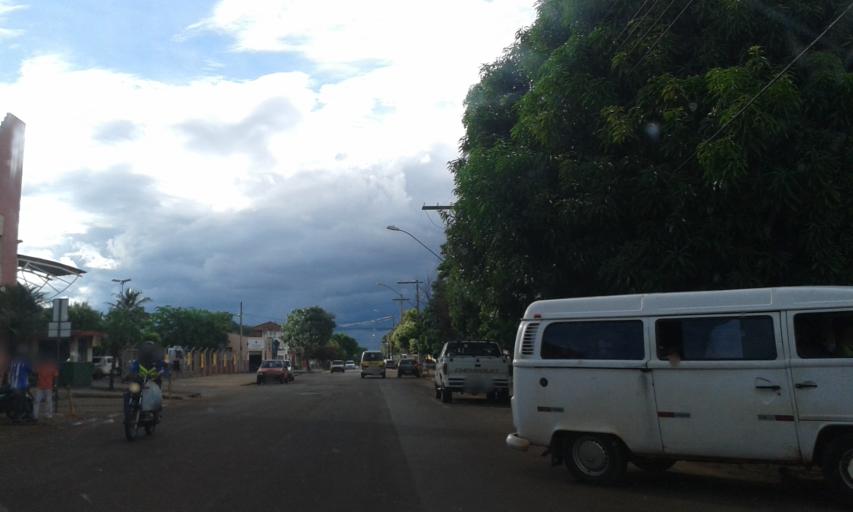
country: BR
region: Minas Gerais
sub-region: Ituiutaba
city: Ituiutaba
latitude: -18.9654
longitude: -49.4504
